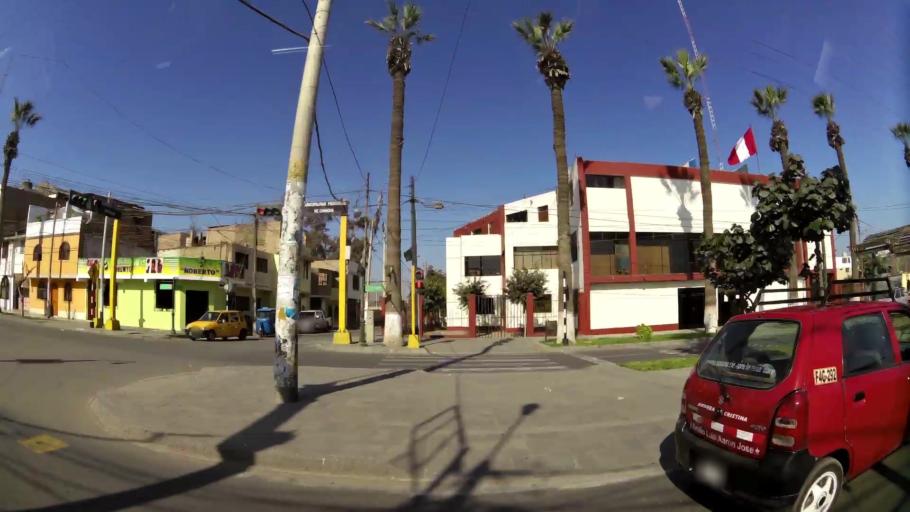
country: PE
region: Ica
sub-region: Provincia de Chincha
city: Chincha Alta
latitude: -13.4137
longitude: -76.1322
